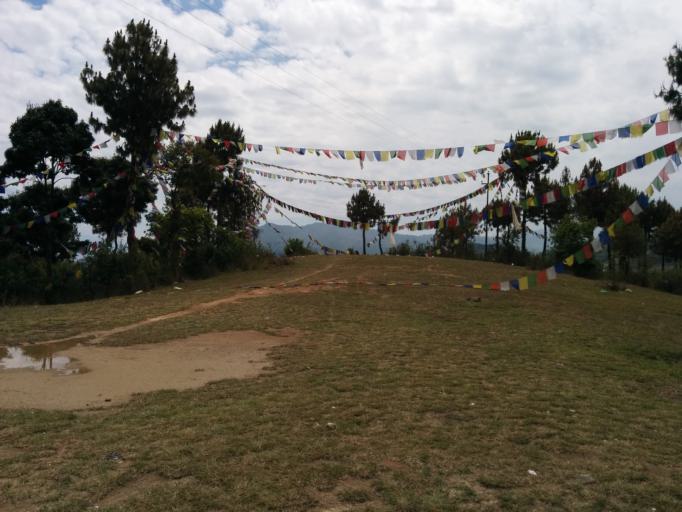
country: NP
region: Central Region
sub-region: Bagmati Zone
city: Nagarkot
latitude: 27.7466
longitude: 85.4989
